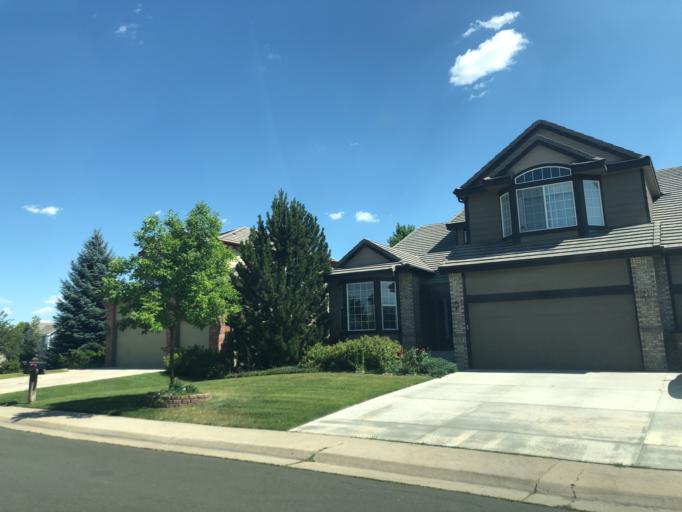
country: US
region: Colorado
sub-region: Arapahoe County
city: Dove Valley
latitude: 39.6042
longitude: -104.7799
